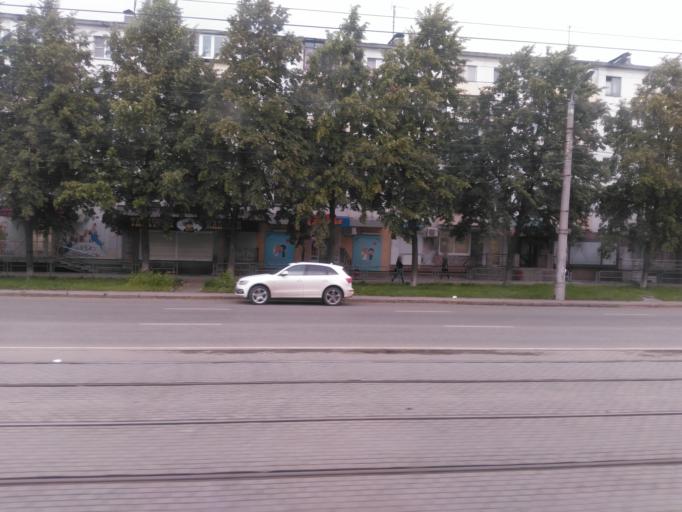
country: RU
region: Chelyabinsk
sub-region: Gorod Chelyabinsk
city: Chelyabinsk
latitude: 55.1819
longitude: 61.3990
